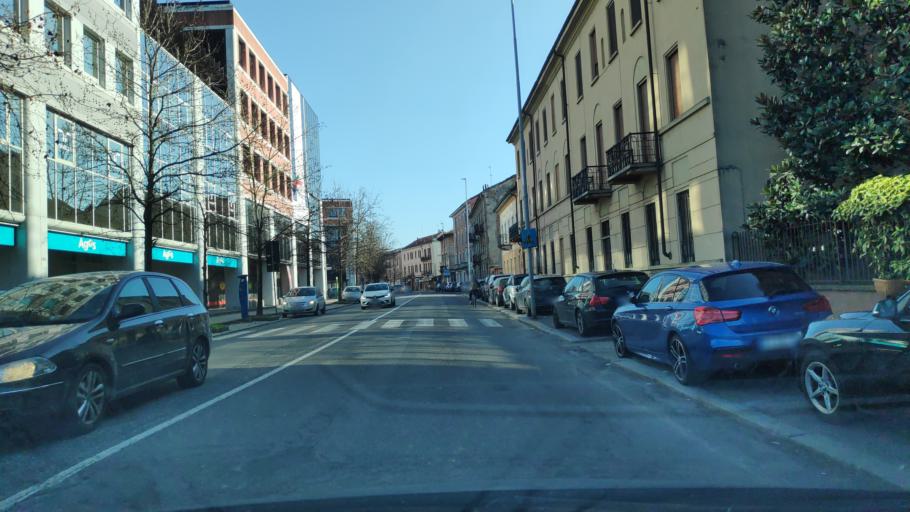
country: IT
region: Lombardy
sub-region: Provincia di Pavia
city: Pavia
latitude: 45.1947
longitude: 9.1536
